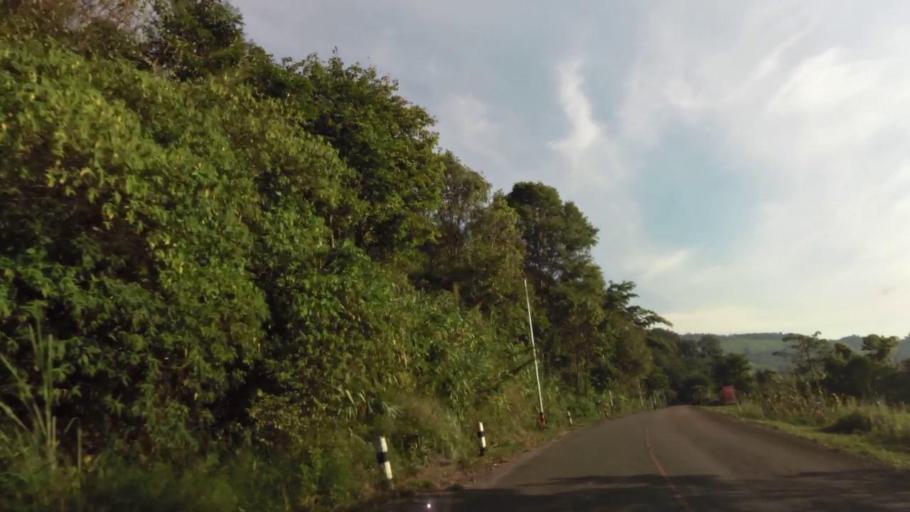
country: TH
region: Chiang Rai
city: Khun Tan
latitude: 19.8548
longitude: 100.4365
